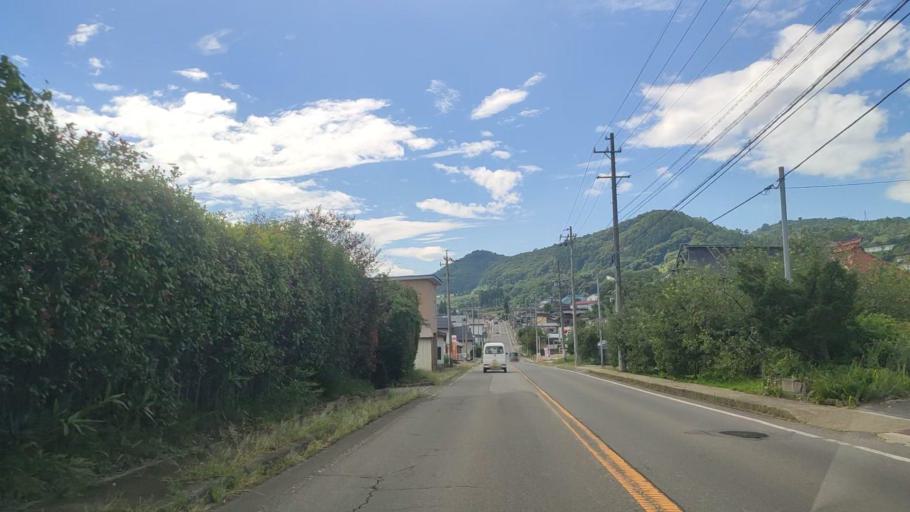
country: JP
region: Nagano
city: Nakano
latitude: 36.7709
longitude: 138.3229
